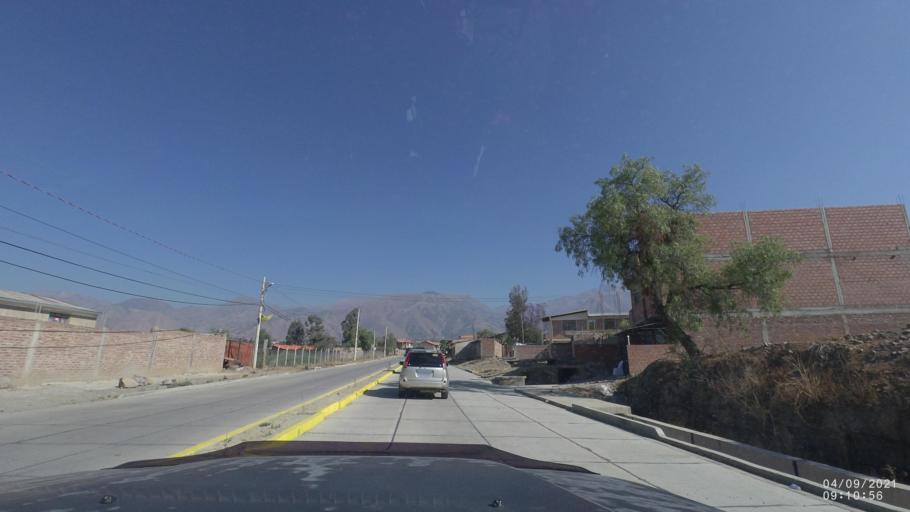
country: BO
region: Cochabamba
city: Sipe Sipe
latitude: -17.3909
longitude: -66.3334
